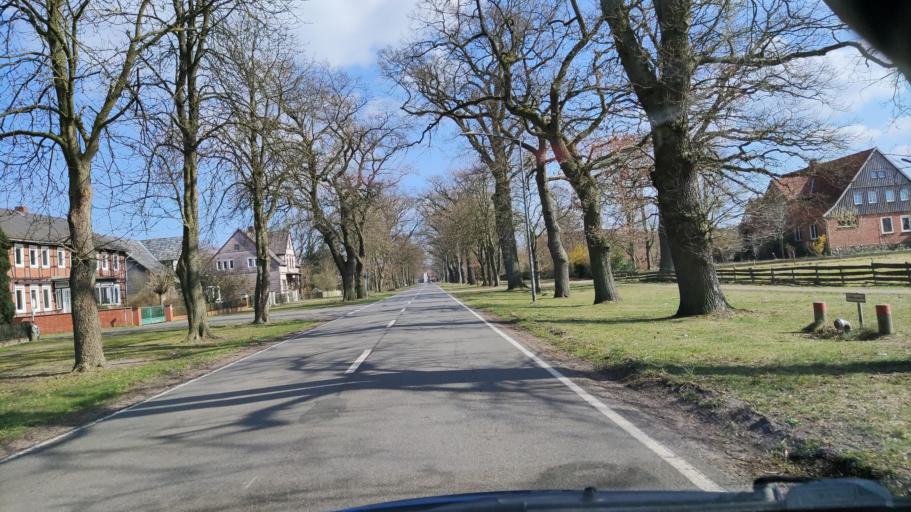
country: DE
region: Lower Saxony
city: Trebel
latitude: 53.0317
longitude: 11.3005
